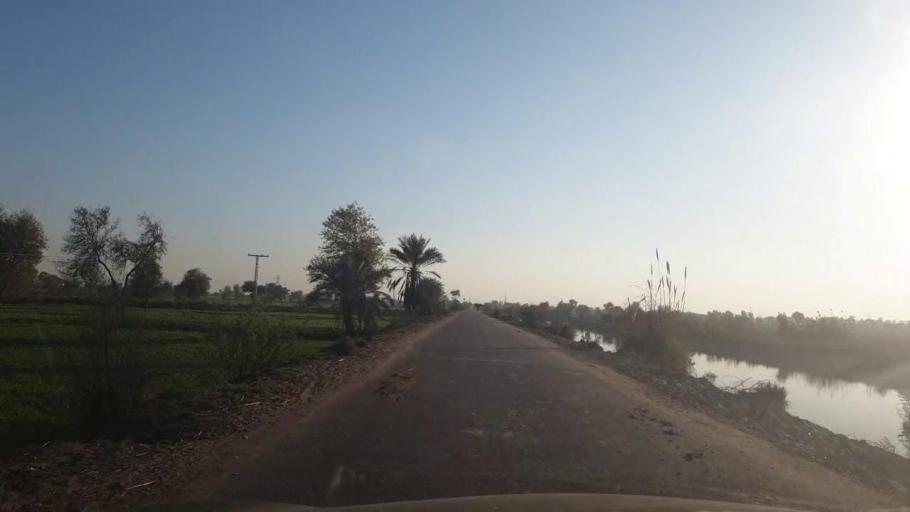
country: PK
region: Sindh
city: Mirpur Mathelo
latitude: 28.0042
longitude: 69.4693
